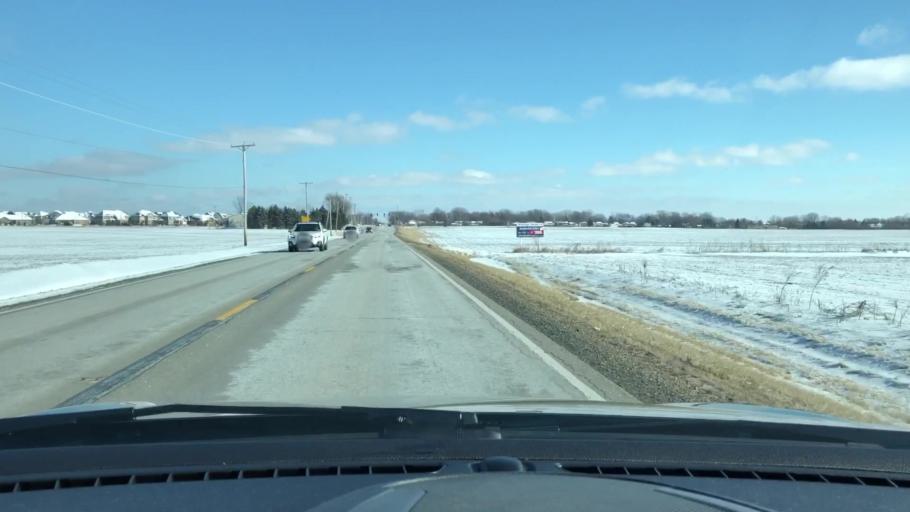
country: US
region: Illinois
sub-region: Will County
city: New Lenox
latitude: 41.4822
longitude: -88.0087
